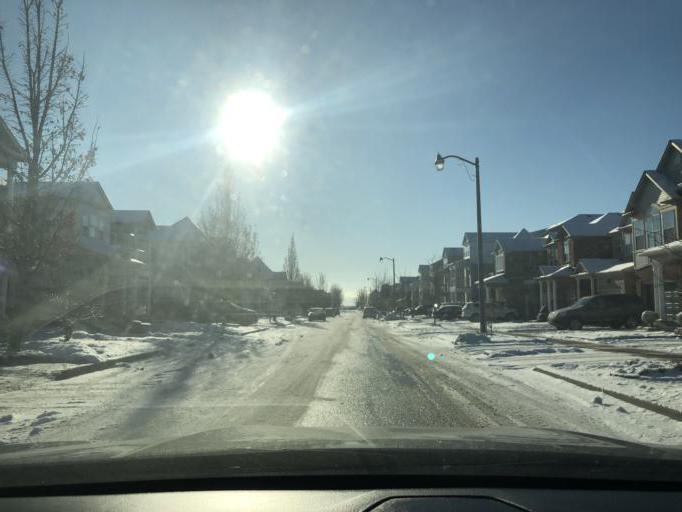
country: CA
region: Ontario
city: Scarborough
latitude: 43.7780
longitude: -79.1375
